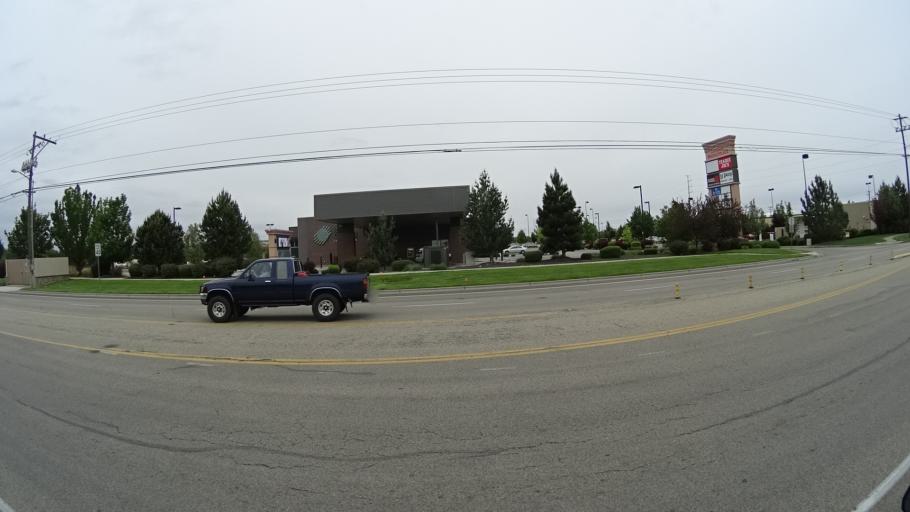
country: US
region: Idaho
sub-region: Ada County
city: Meridian
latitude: 43.6339
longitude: -116.3523
